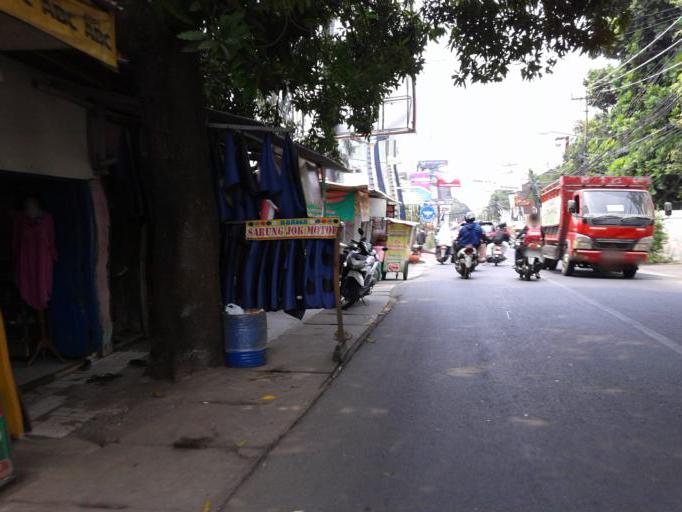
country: ID
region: Banten
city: South Tangerang
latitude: -6.2956
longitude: 106.7577
